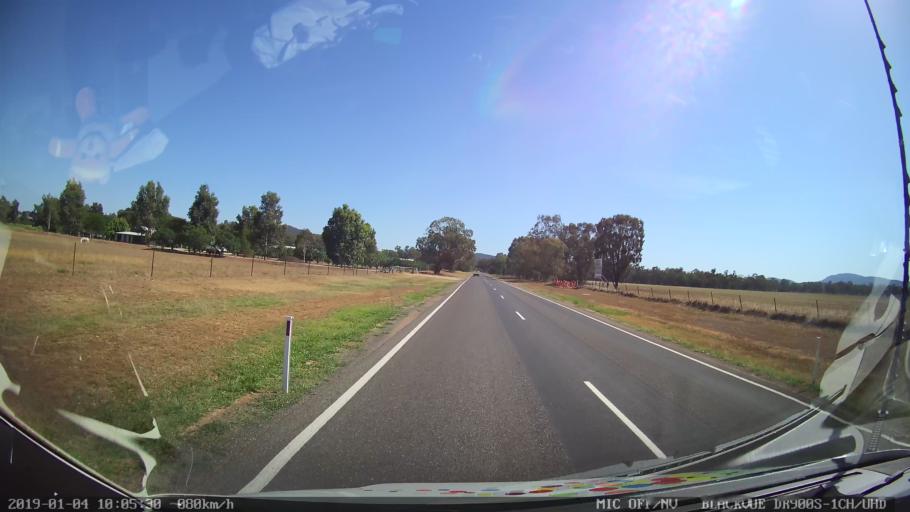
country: AU
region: New South Wales
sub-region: Cabonne
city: Canowindra
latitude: -33.4409
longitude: 148.3654
